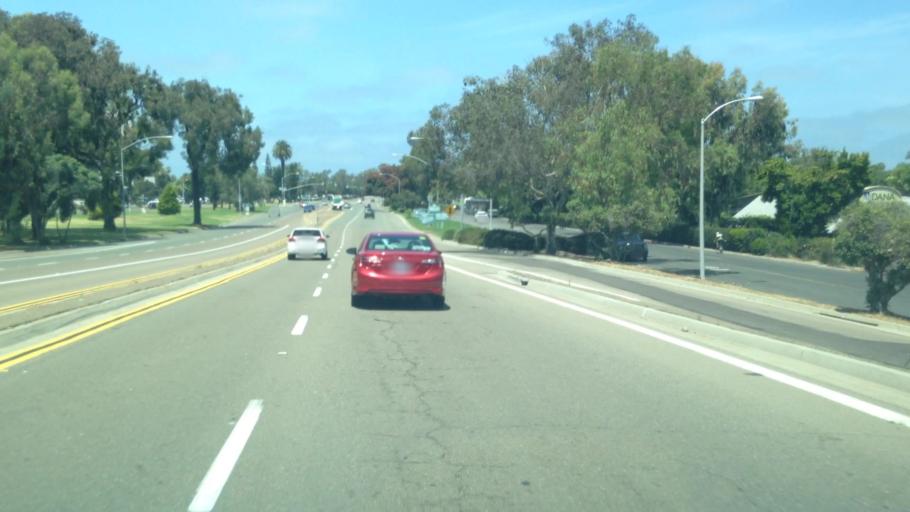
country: US
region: California
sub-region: San Diego County
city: San Diego
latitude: 32.7645
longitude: -117.2344
